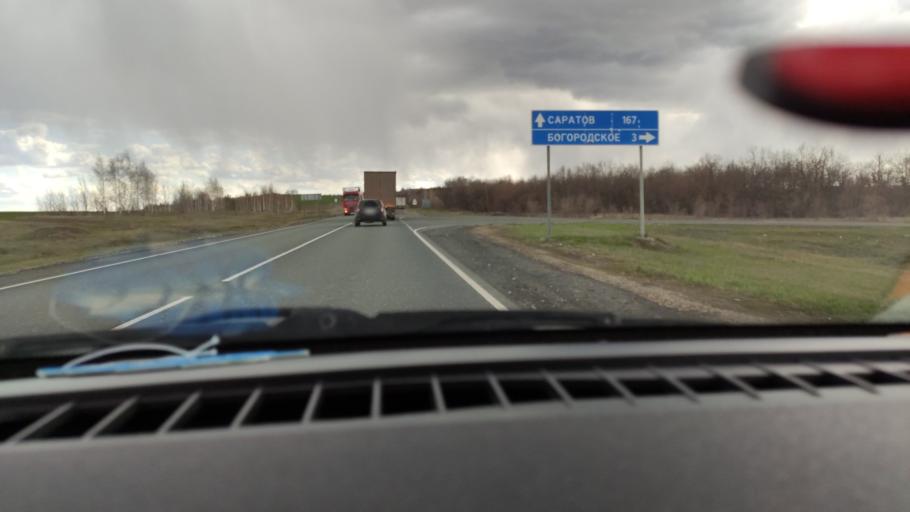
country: RU
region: Saratov
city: Balakovo
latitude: 52.1743
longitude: 47.8345
